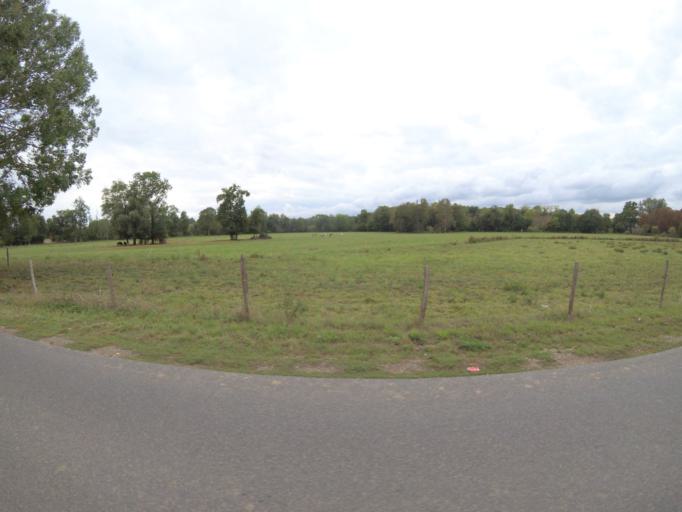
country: FR
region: Ile-de-France
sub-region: Departement de Seine-et-Marne
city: Saint-Thibault-des-Vignes
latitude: 48.8605
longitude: 2.6778
